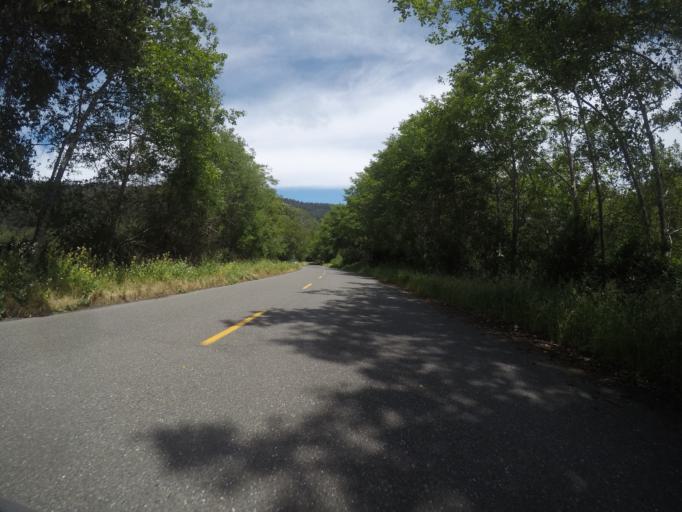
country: US
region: California
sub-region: Humboldt County
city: Westhaven-Moonstone
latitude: 41.3001
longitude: -124.0442
